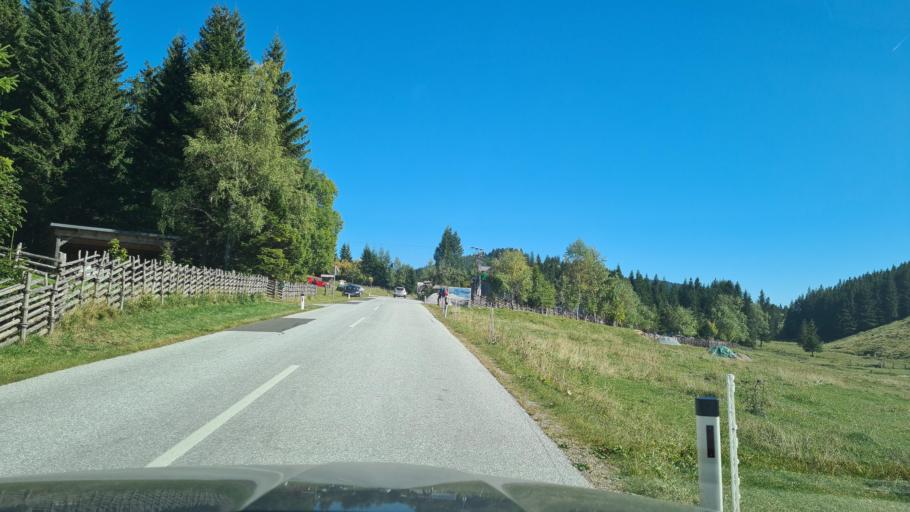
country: AT
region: Styria
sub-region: Politischer Bezirk Weiz
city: Gasen
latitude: 47.3526
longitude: 15.5072
